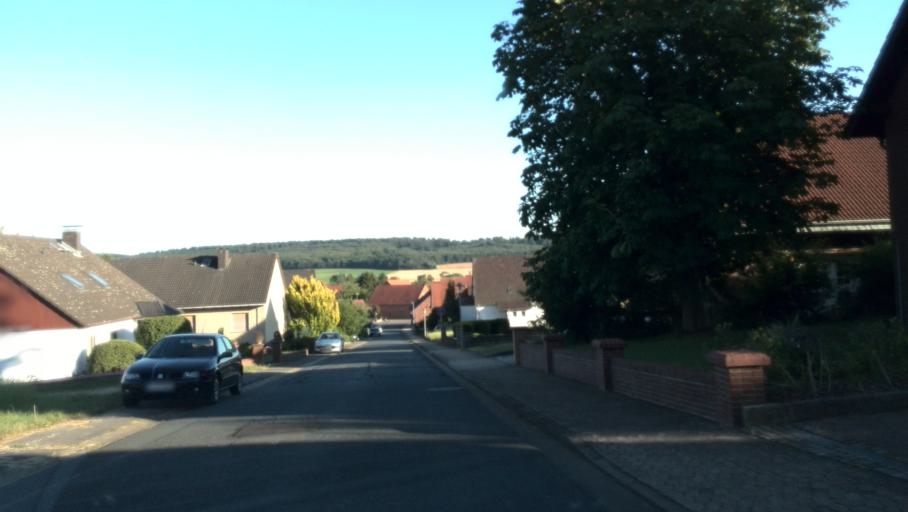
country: DE
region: Lower Saxony
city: Holle
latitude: 52.1090
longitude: 10.1020
